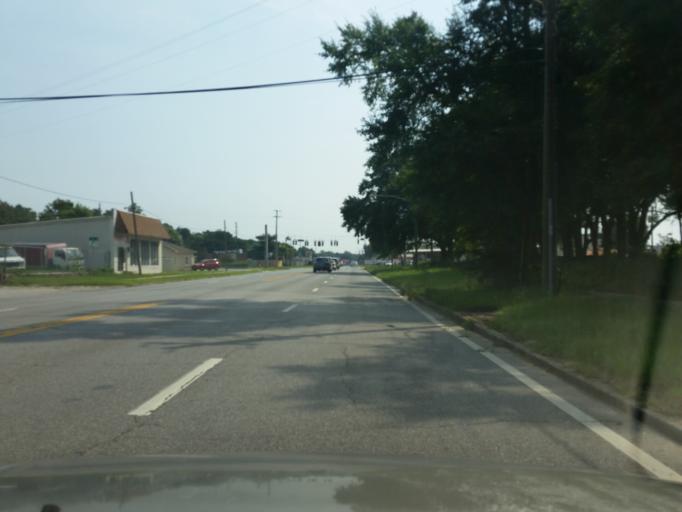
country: US
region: Florida
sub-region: Escambia County
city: Pensacola
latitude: 30.4067
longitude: -87.2367
